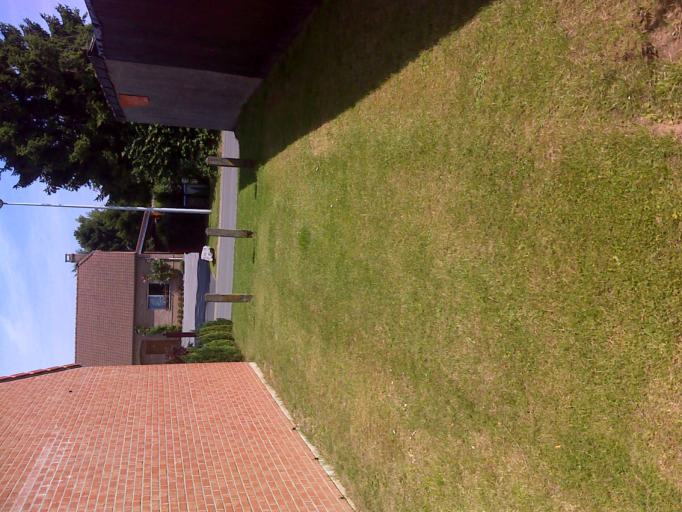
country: FR
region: Nord-Pas-de-Calais
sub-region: Departement du Nord
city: Aulnoye-Aymeries
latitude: 50.2048
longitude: 3.8500
